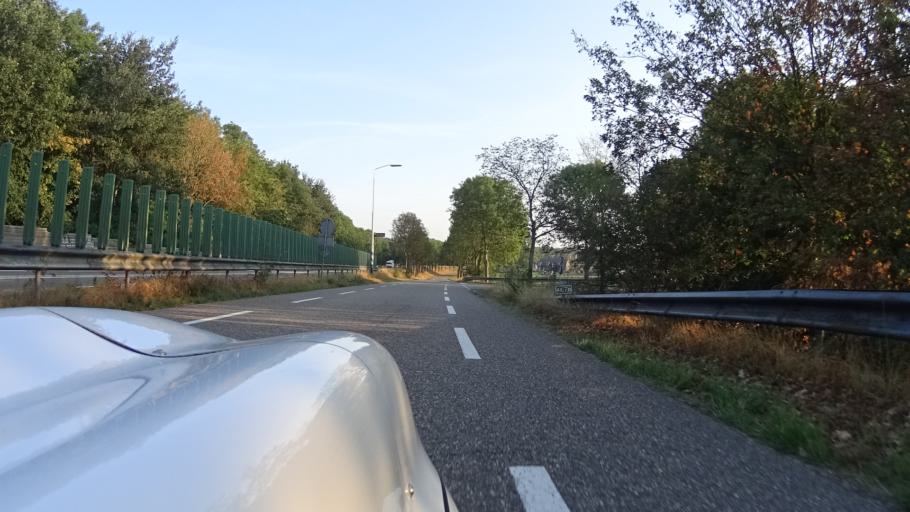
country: NL
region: Limburg
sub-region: Gemeente Bergen
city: Wellerlooi
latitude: 51.5507
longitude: 6.0987
